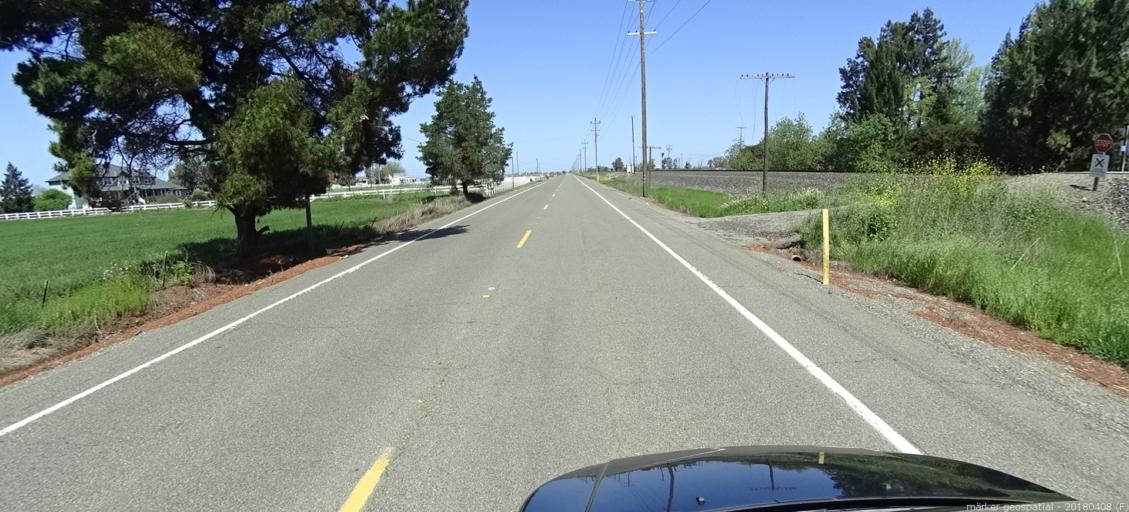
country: US
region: California
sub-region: Sacramento County
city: Laguna
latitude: 38.3272
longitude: -121.4453
